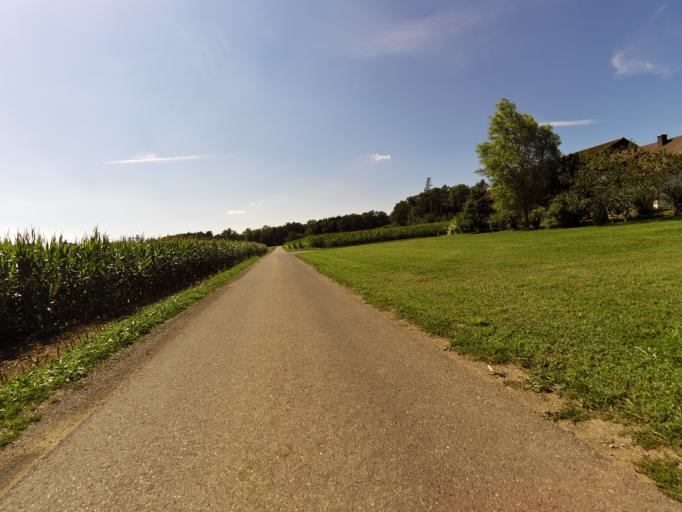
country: CH
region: Thurgau
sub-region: Weinfelden District
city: Maerstetten-Dorf
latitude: 47.6280
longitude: 9.0655
